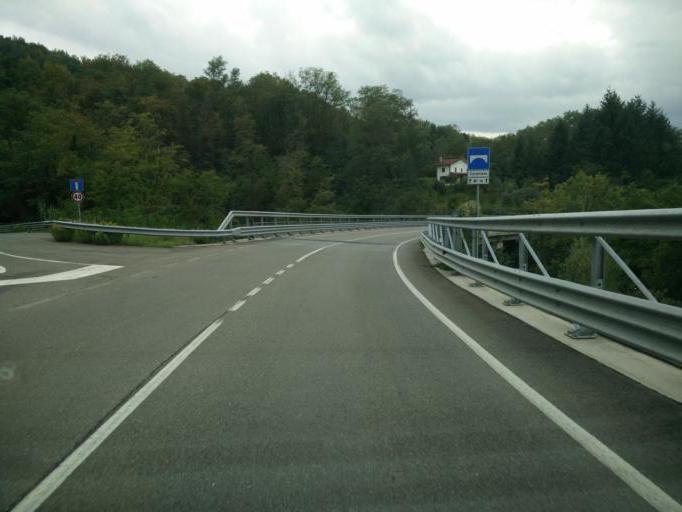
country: IT
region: Tuscany
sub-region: Provincia di Massa-Carrara
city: Fivizzano
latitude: 44.2257
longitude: 10.1157
